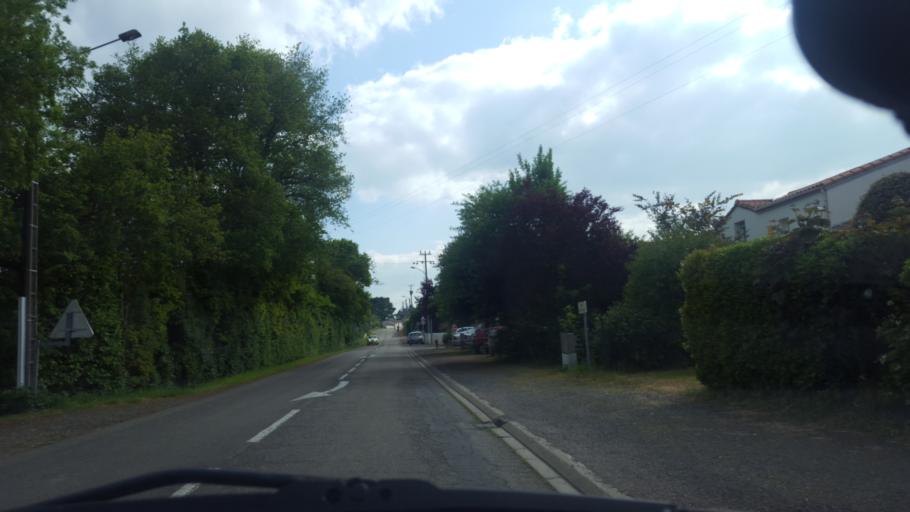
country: FR
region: Pays de la Loire
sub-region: Departement de la Loire-Atlantique
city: La Limouziniere
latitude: 46.9968
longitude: -1.5926
